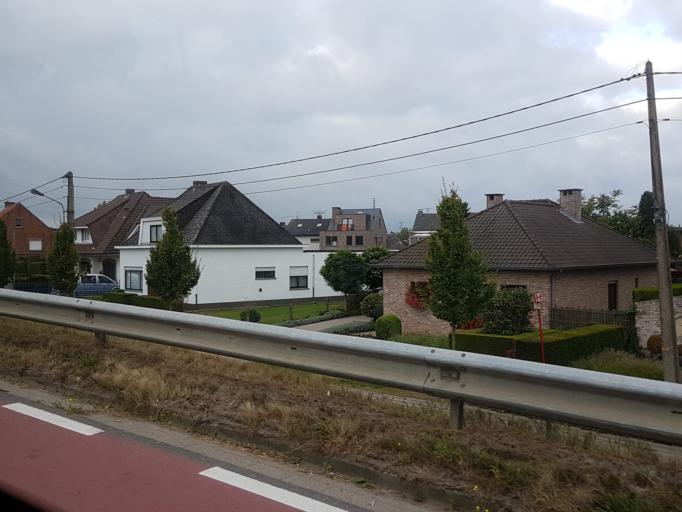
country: BE
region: Flanders
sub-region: Provincie Antwerpen
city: Zandhoven
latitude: 51.1985
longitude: 4.6423
